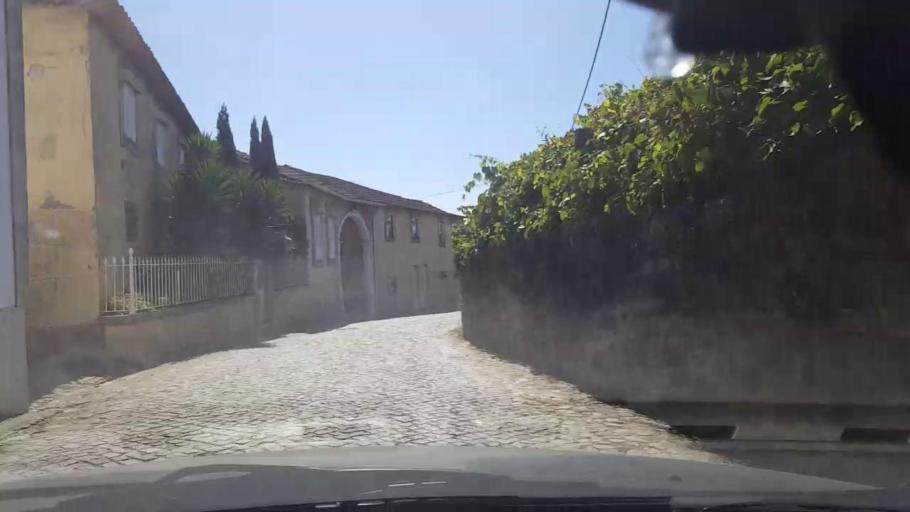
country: PT
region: Porto
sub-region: Matosinhos
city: Lavra
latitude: 41.2862
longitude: -8.6854
